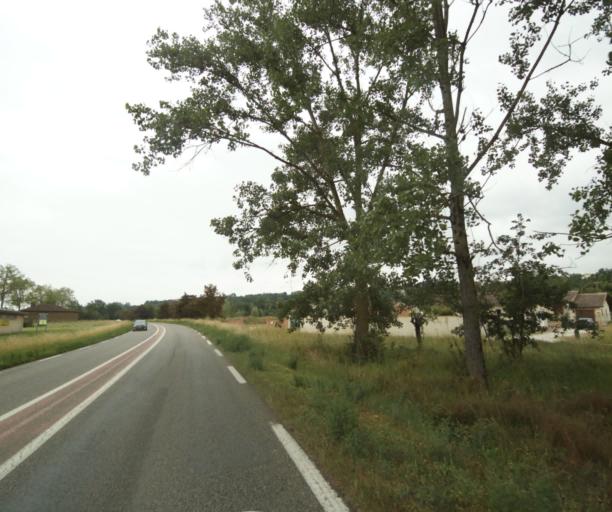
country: FR
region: Midi-Pyrenees
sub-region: Departement du Tarn-et-Garonne
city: Saint-Nauphary
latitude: 43.9810
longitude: 1.3937
